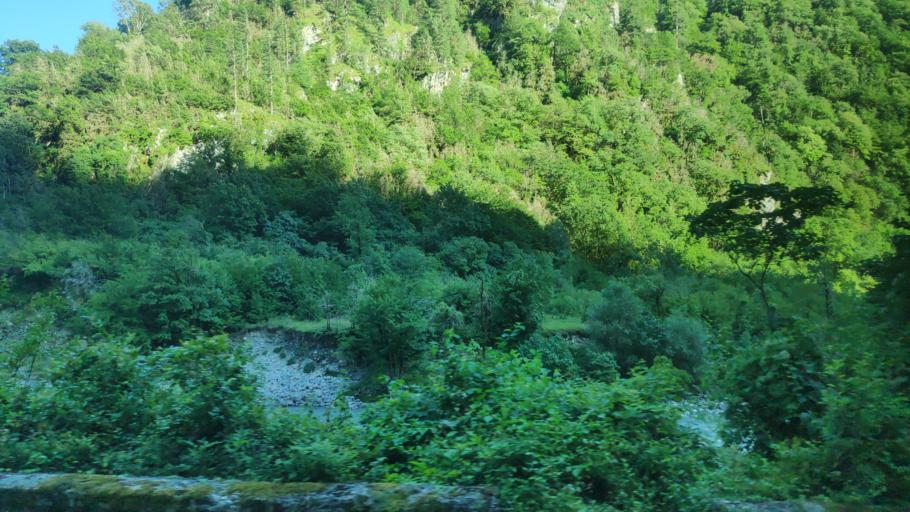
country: GE
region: Abkhazia
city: Gagra
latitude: 43.3682
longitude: 40.4571
